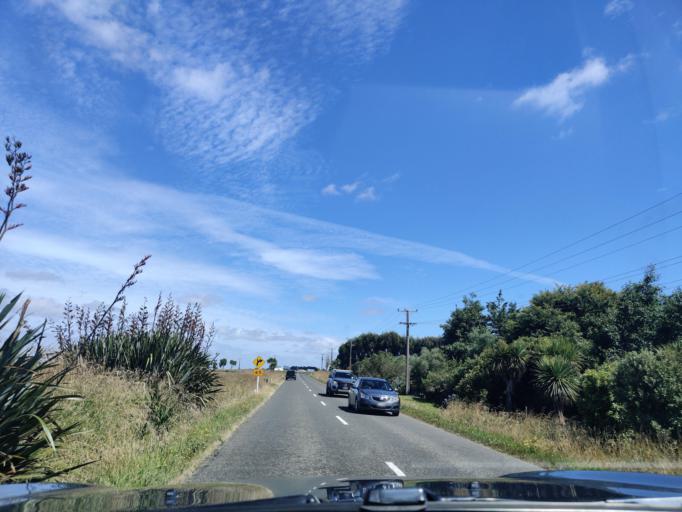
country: NZ
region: Manawatu-Wanganui
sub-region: Rangitikei District
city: Bulls
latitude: -40.1941
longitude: 175.4776
